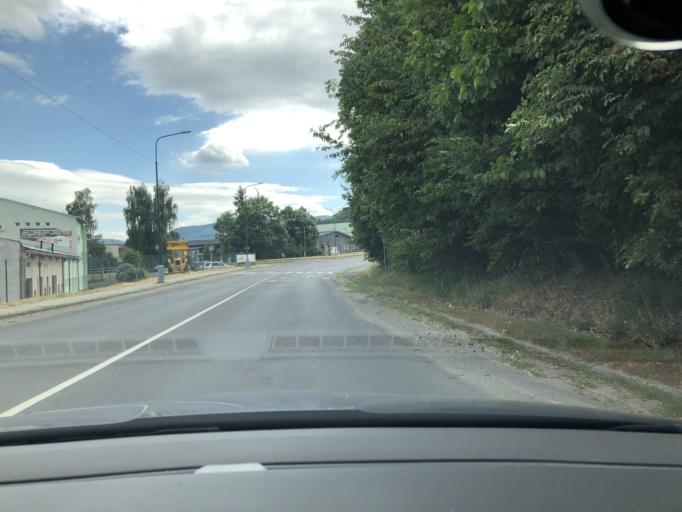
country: SK
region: Banskobystricky
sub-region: Okres Banska Bystrica
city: Banska Stiavnica
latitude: 48.4506
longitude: 18.9122
